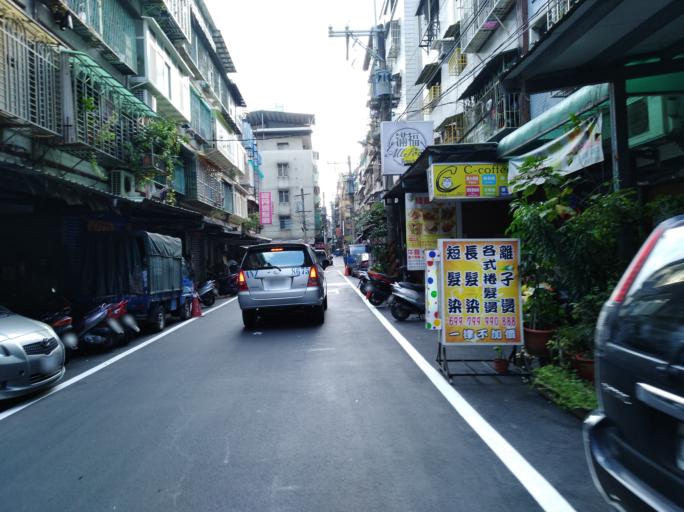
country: TW
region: Taipei
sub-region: Taipei
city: Banqiao
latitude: 25.0405
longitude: 121.4256
